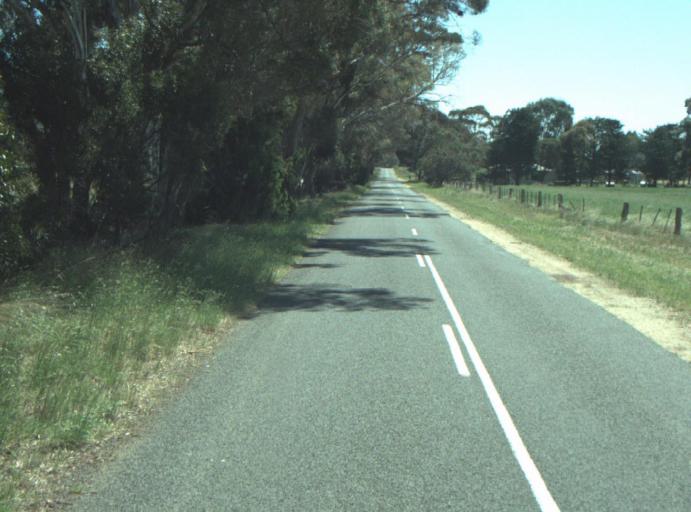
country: AU
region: Victoria
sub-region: Greater Geelong
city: Lara
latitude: -37.8662
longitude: 144.2787
